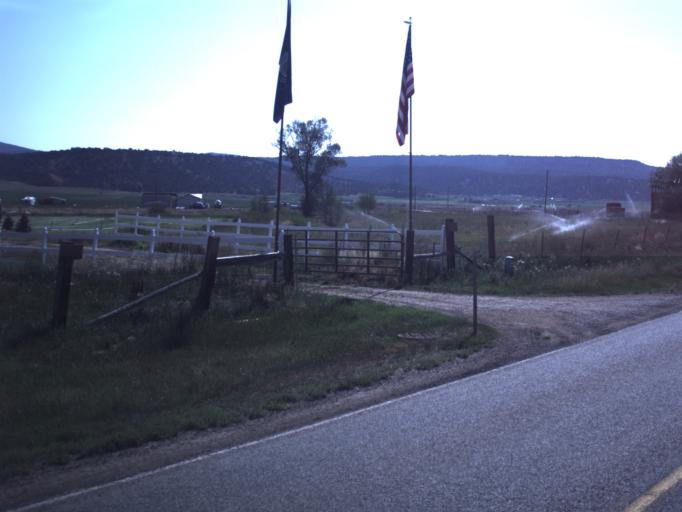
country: US
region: Utah
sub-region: Duchesne County
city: Duchesne
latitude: 40.3442
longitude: -110.6980
